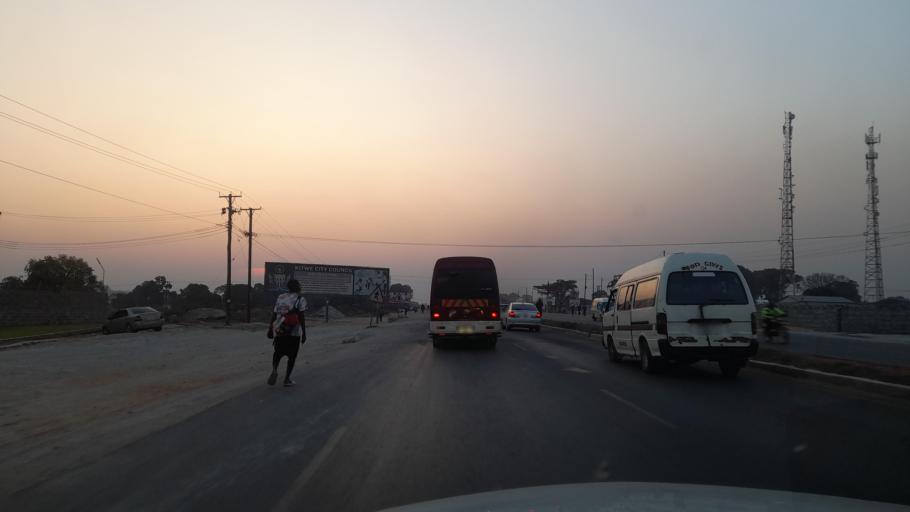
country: ZM
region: Copperbelt
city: Kitwe
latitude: -12.7749
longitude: 28.1904
